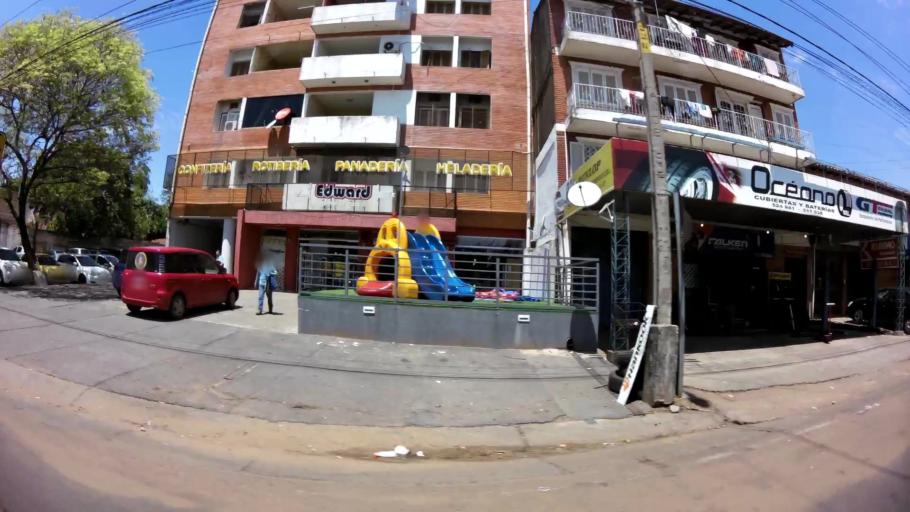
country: PY
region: Central
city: Lambare
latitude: -25.3378
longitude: -57.5829
